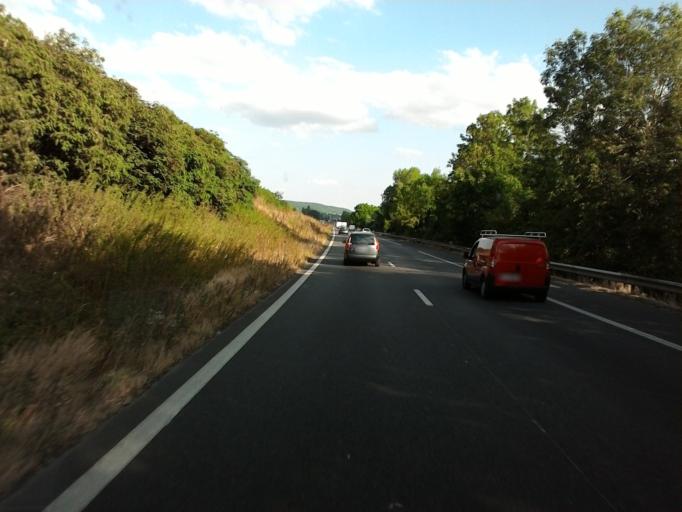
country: FR
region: Lorraine
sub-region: Departement de Meurthe-et-Moselle
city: Frouard
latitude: 48.7634
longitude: 6.1456
